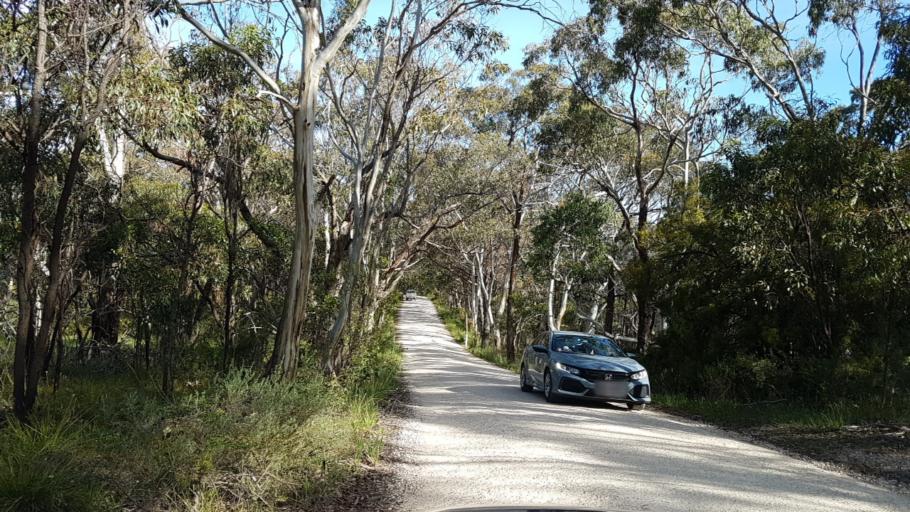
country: AU
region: South Australia
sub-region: Adelaide Hills
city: Adelaide Hills
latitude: -34.9084
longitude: 138.7488
